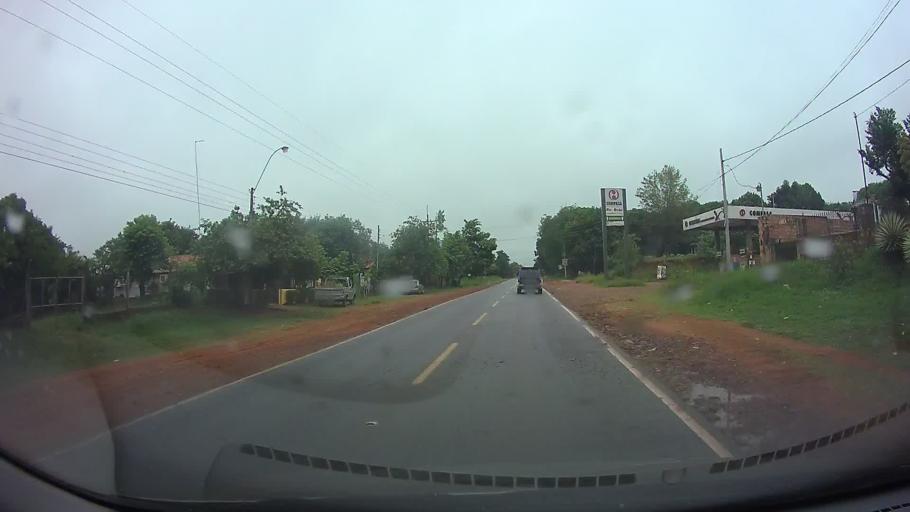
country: PY
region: Central
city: Itaugua
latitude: -25.4255
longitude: -57.3640
